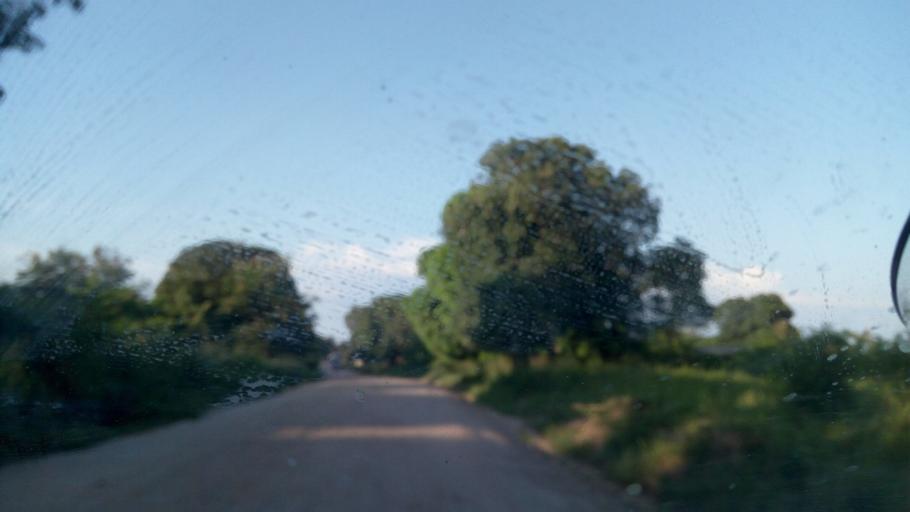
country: BI
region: Bururi
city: Rumonge
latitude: -4.1230
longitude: 29.0832
